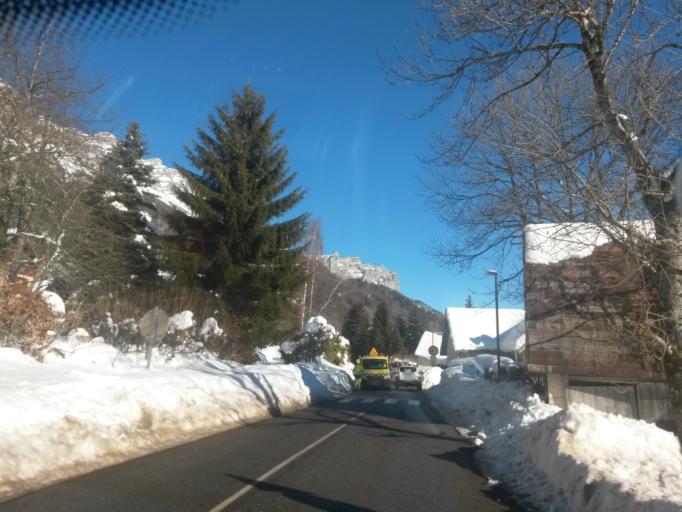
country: FR
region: Rhone-Alpes
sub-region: Departement de l'Isere
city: Saint-Hilaire
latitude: 45.3145
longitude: 5.8879
